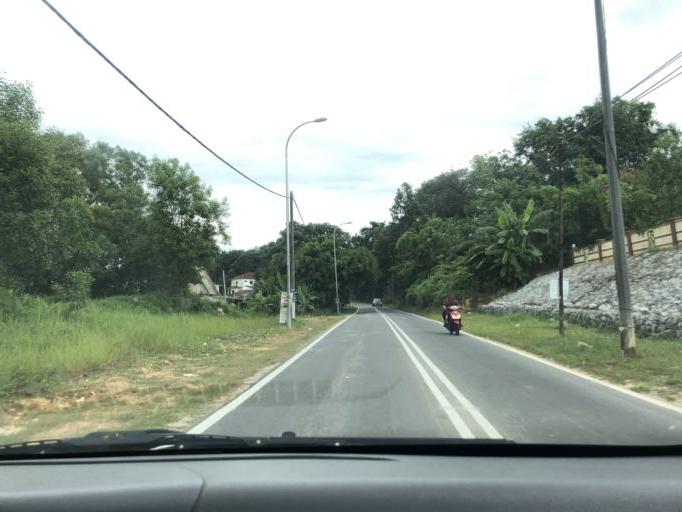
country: MY
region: Putrajaya
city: Putrajaya
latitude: 2.9193
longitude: 101.7497
